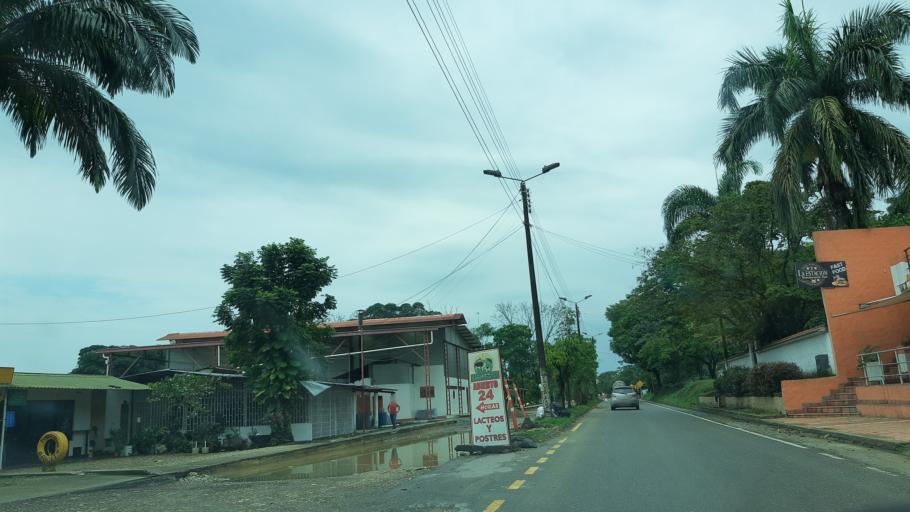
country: CO
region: Casanare
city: Monterrey
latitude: 4.8370
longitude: -72.9562
